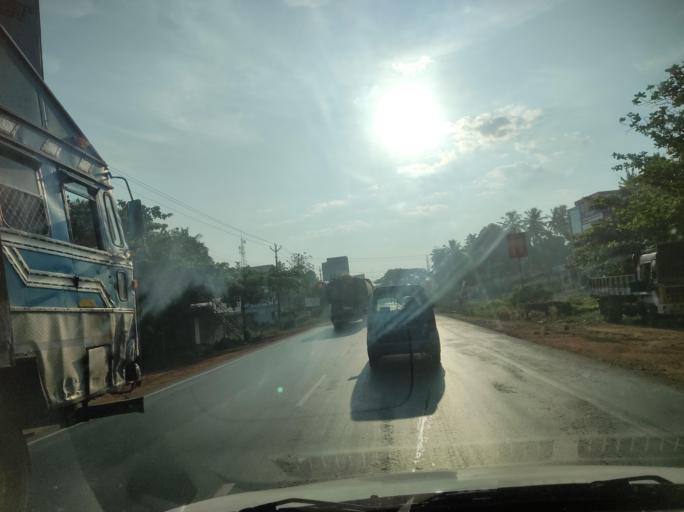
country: IN
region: Kerala
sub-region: Alappuzha
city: Mavelikara
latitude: 9.2817
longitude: 76.4551
